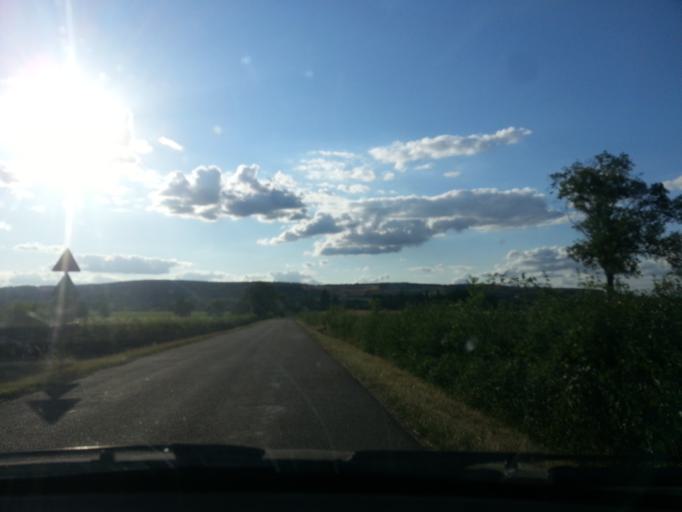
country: FR
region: Bourgogne
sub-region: Departement de Saone-et-Loire
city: Givry
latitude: 46.7740
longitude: 4.7638
